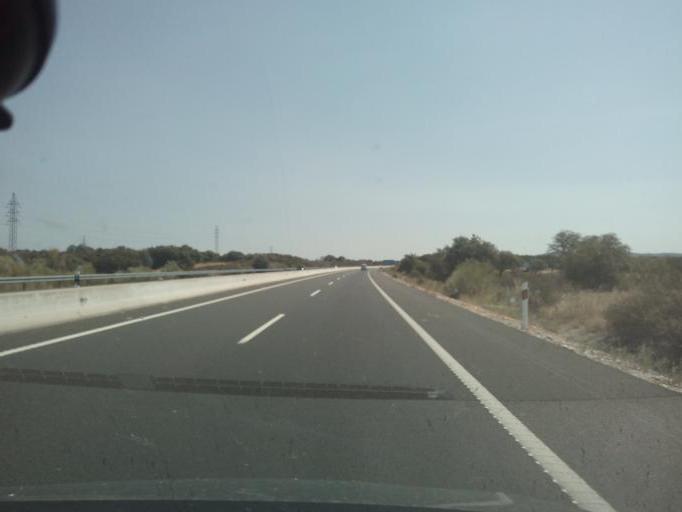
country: ES
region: Extremadura
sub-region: Provincia de Caceres
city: Romangordo
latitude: 39.7852
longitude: -5.7240
